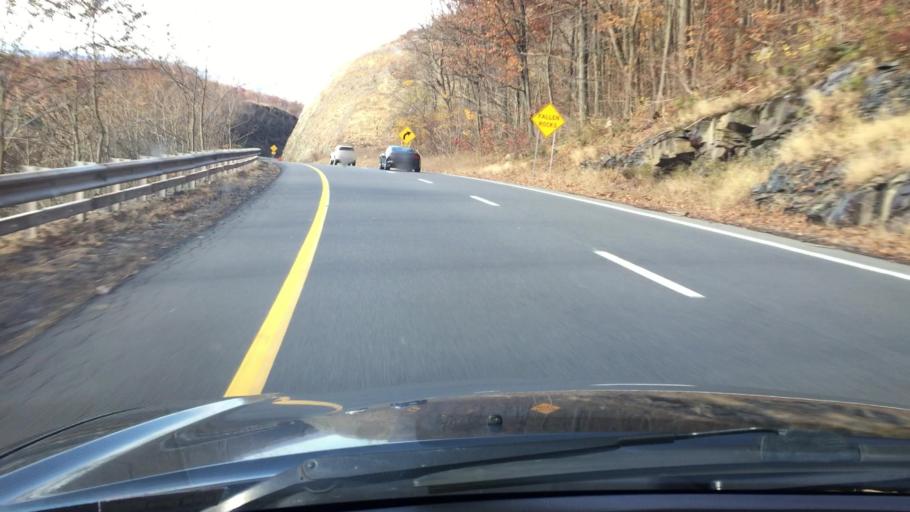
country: US
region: Pennsylvania
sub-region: Luzerne County
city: Mountain Top
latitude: 41.1856
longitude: -75.8904
